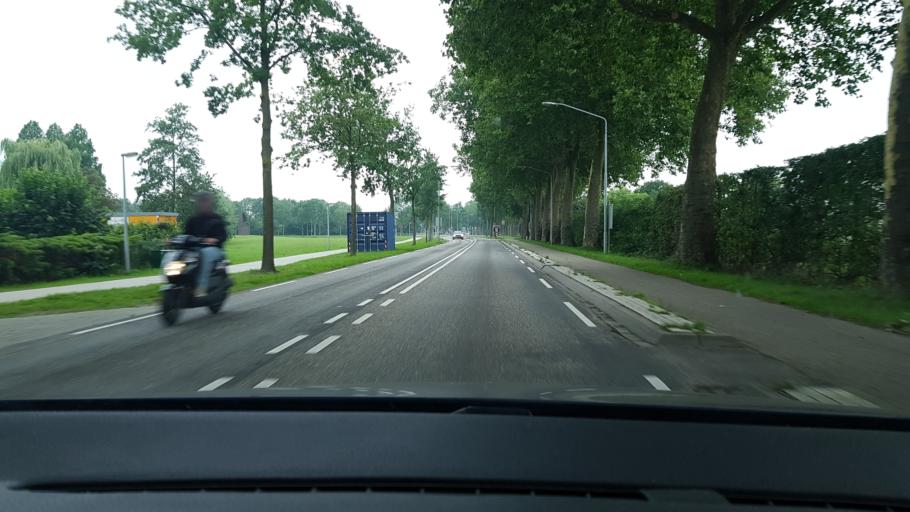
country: NL
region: Gelderland
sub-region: Gemeente Beuningen
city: Beuningen
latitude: 51.8691
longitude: 5.7591
